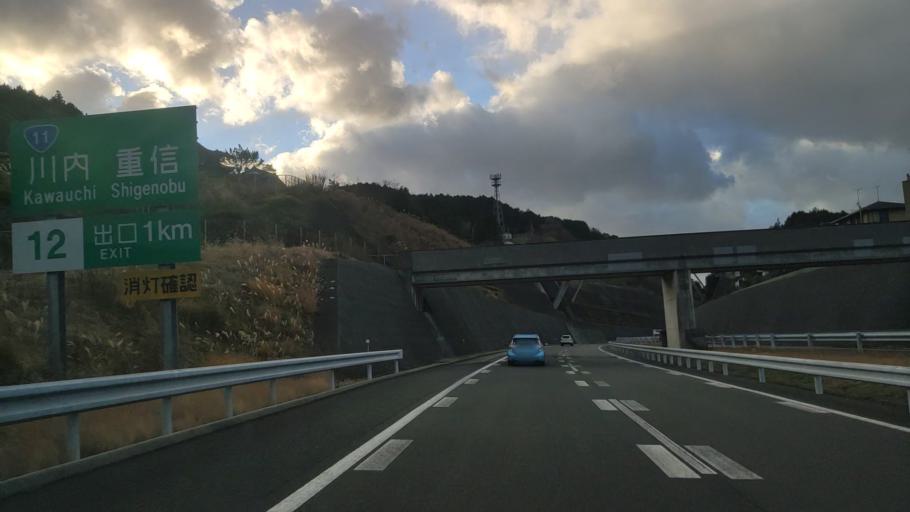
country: JP
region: Ehime
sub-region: Shikoku-chuo Shi
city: Matsuyama
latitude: 33.7903
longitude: 132.9183
